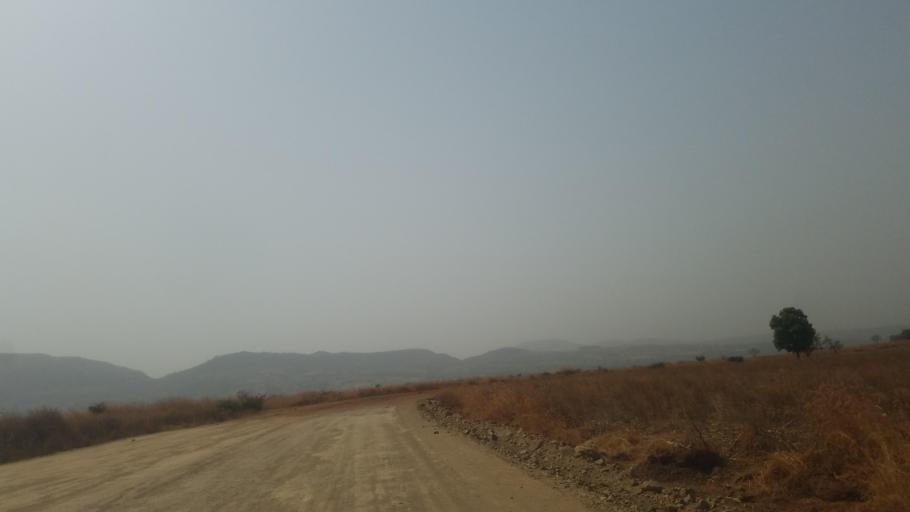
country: ET
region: Amhara
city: Bure
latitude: 10.9003
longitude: 36.4657
